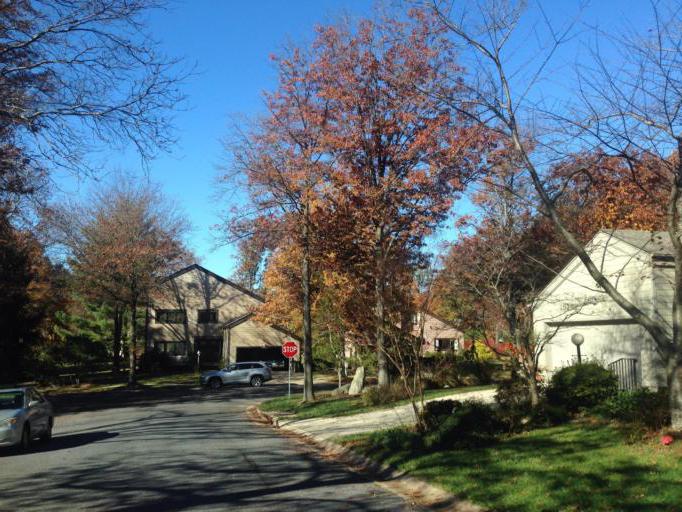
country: US
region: Maryland
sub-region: Howard County
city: Riverside
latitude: 39.1959
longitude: -76.8706
